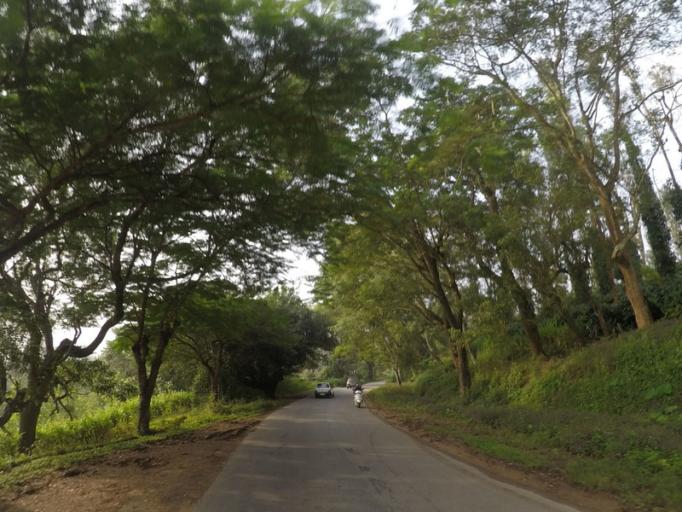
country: IN
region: Karnataka
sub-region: Chikmagalur
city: Chikmagalur
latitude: 13.2610
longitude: 75.6802
